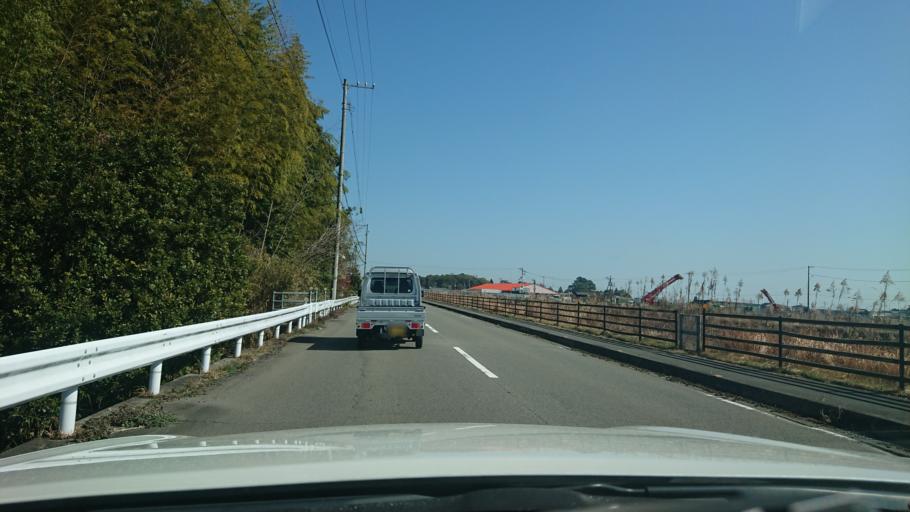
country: JP
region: Tokushima
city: Komatsushimacho
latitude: 33.9725
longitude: 134.6007
